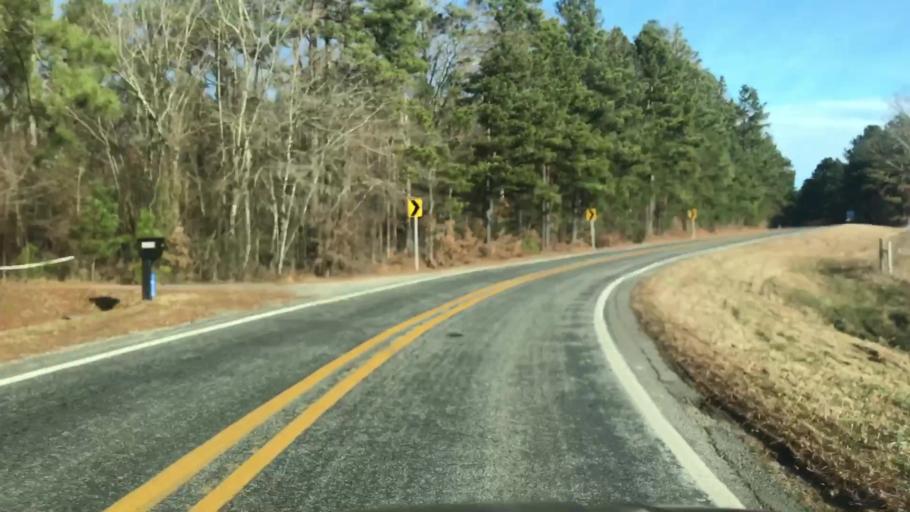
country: US
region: Arkansas
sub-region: Garland County
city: Rockwell
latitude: 34.4814
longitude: -93.2734
